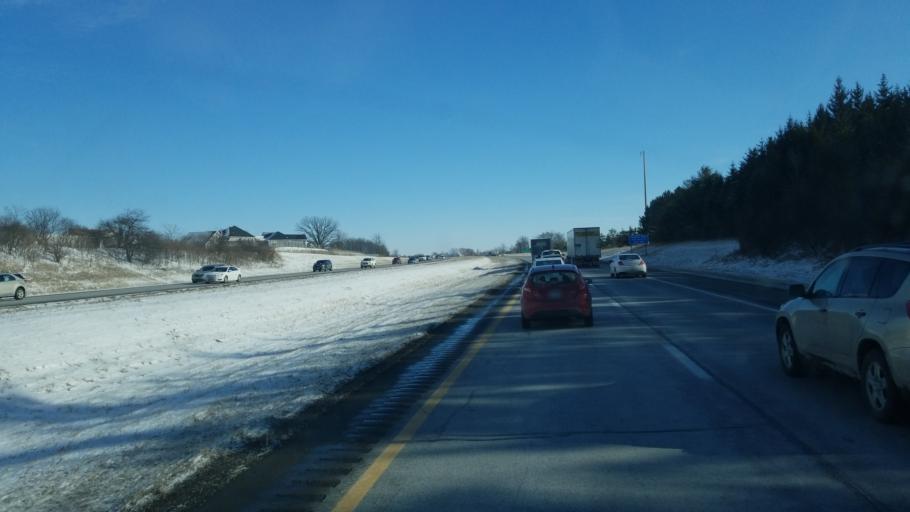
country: US
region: Ohio
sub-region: Lucas County
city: Maumee
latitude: 41.5369
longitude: -83.6742
